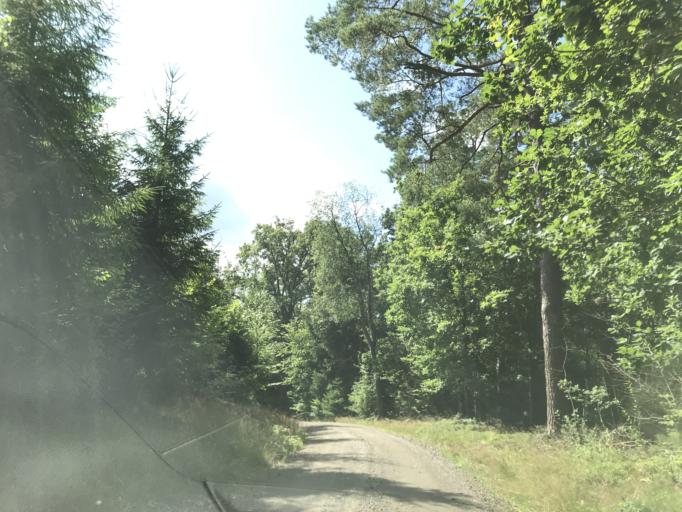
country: SE
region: Halland
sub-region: Laholms Kommun
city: Knared
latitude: 56.5104
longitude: 13.2944
